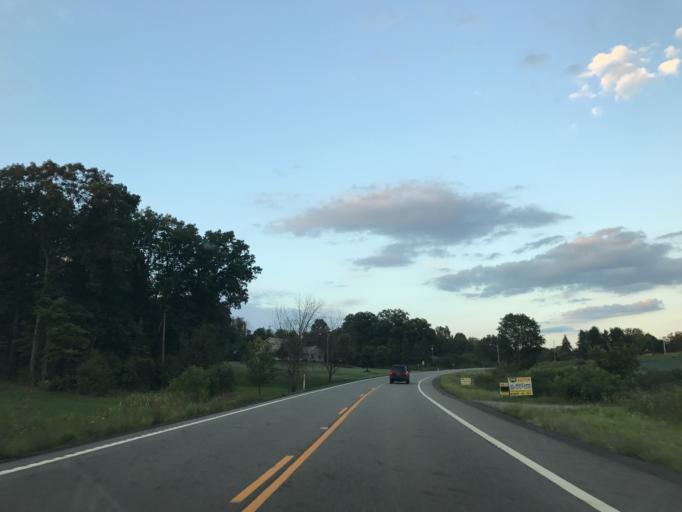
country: US
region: Ohio
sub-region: Columbiana County
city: Lisbon
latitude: 40.7684
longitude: -80.8630
